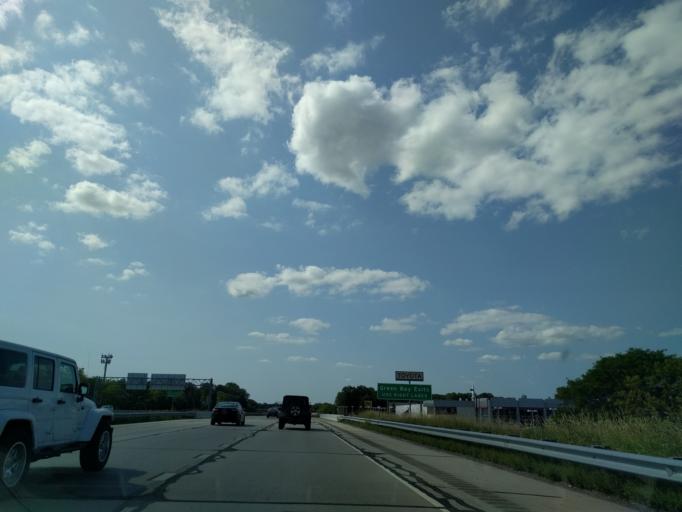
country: US
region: Wisconsin
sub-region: Brown County
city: Ashwaubenon
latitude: 44.4806
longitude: -88.0699
